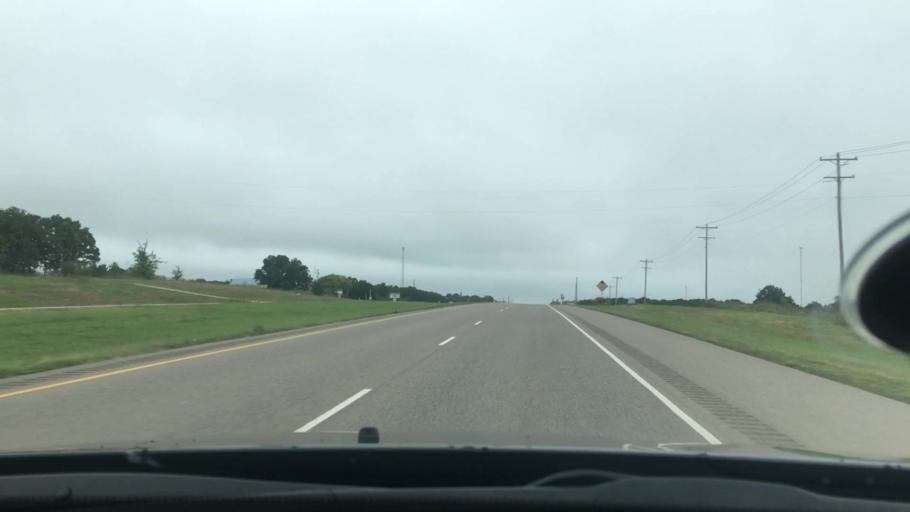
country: US
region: Oklahoma
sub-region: Lincoln County
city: Prague
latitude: 35.3686
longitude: -96.6714
